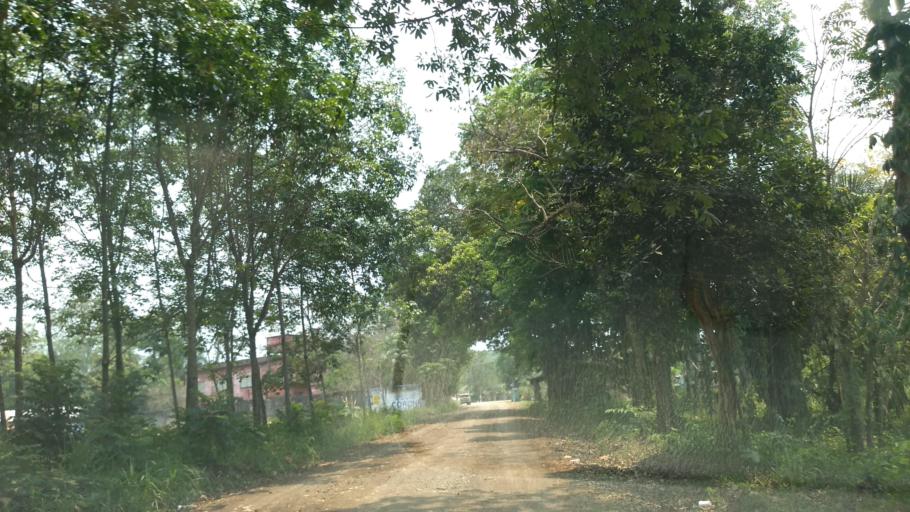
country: MX
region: Veracruz
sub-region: Tezonapa
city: Laguna Chica (Pueblo Nuevo)
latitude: 18.5115
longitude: -96.7673
